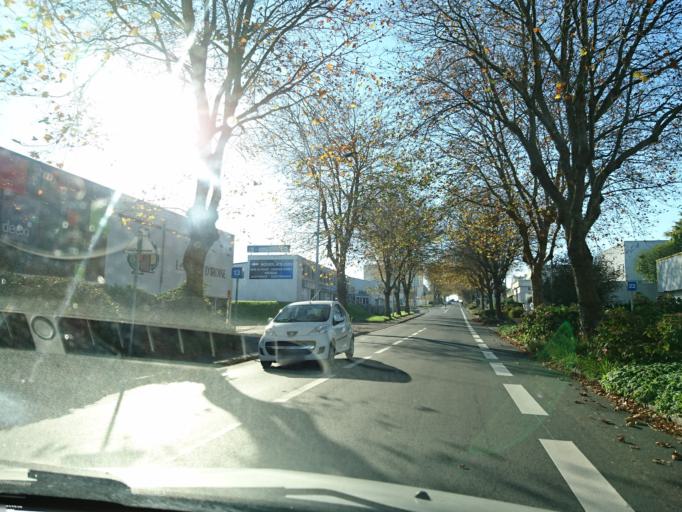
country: FR
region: Brittany
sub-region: Departement du Finistere
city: Brest
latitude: 48.4114
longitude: -4.4577
